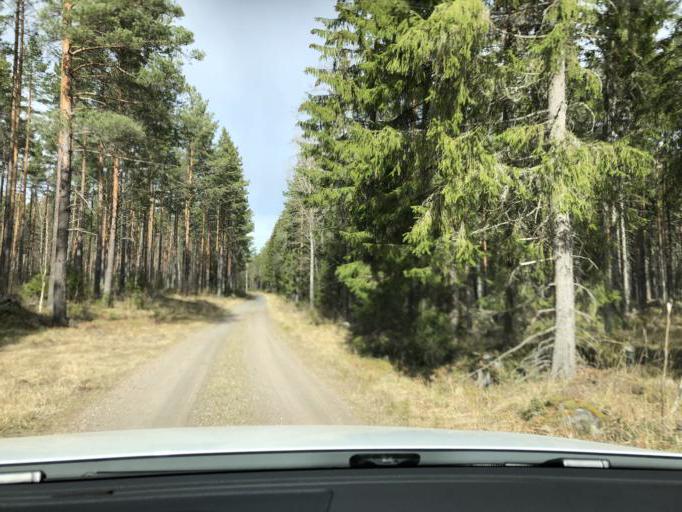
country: SE
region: Gaevleborg
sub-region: Gavle Kommun
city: Hedesunda
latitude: 60.3299
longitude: 17.1068
